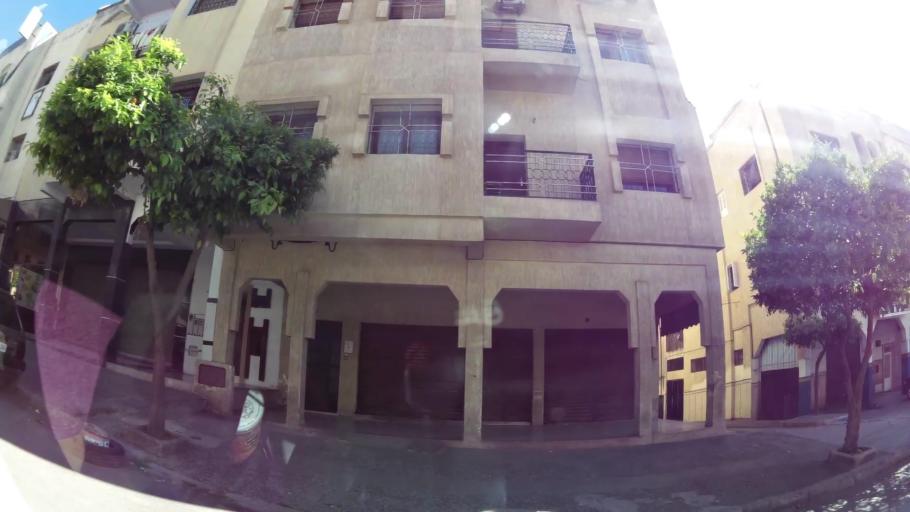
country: MA
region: Fes-Boulemane
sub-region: Fes
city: Fes
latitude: 34.0188
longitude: -4.9835
